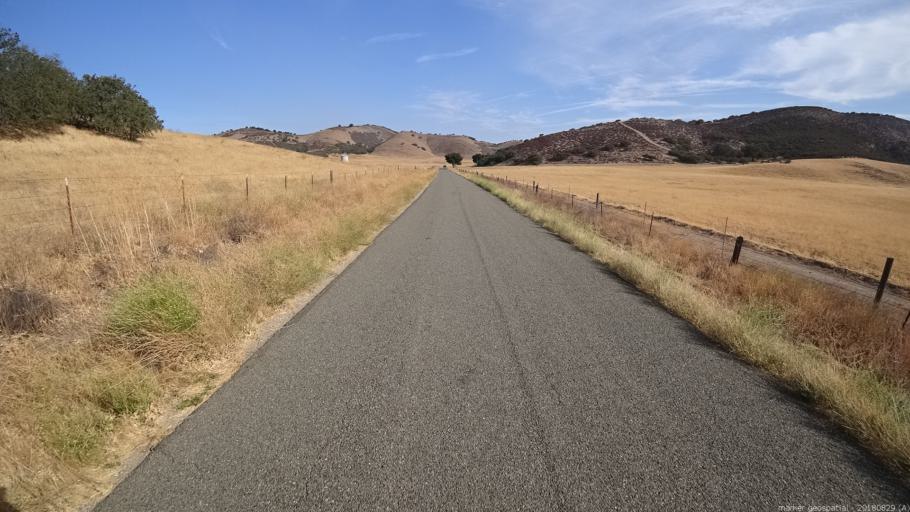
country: US
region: California
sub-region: Monterey County
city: King City
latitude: 36.0520
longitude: -121.0523
